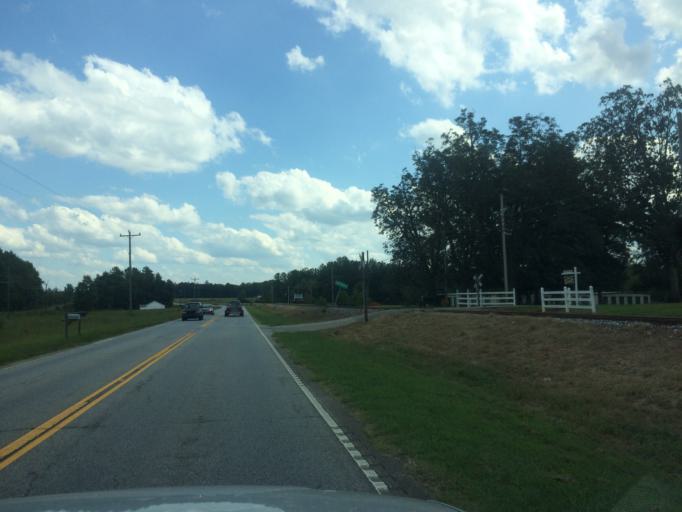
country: US
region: South Carolina
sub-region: Anderson County
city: Belton
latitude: 34.5106
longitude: -82.4757
